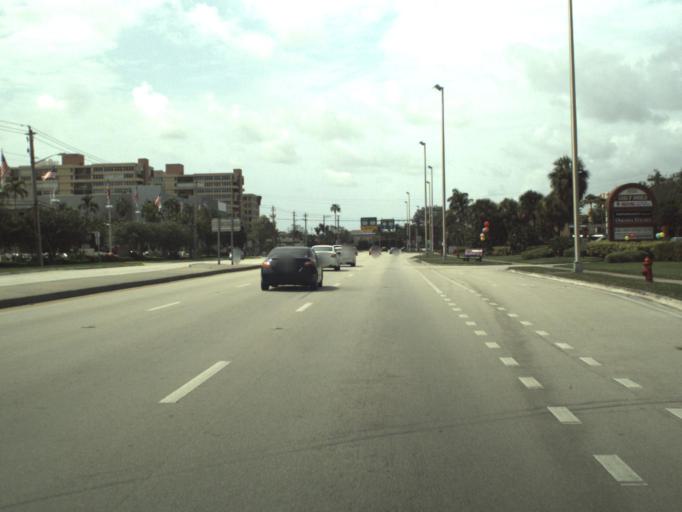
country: US
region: Florida
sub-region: Broward County
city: Sunrise
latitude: 26.1422
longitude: -80.1202
